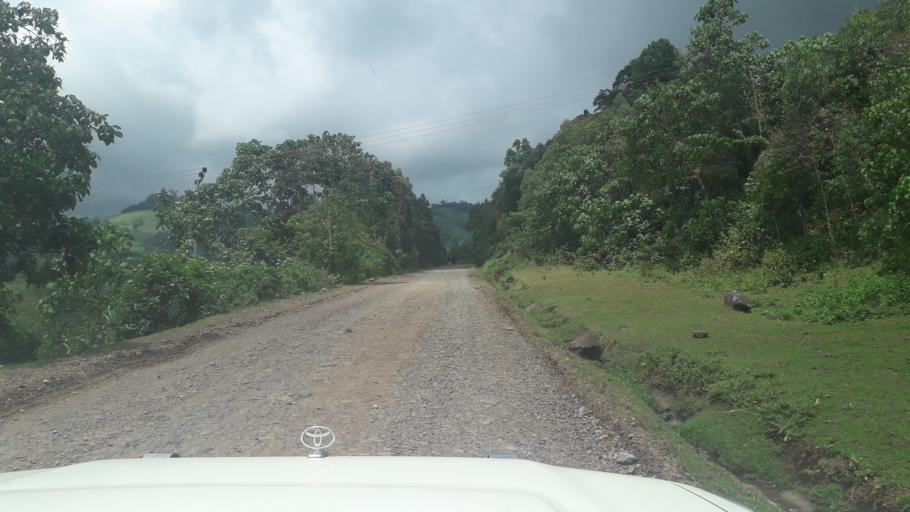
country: ET
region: Oromiya
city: Jima
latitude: 7.4313
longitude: 36.8755
